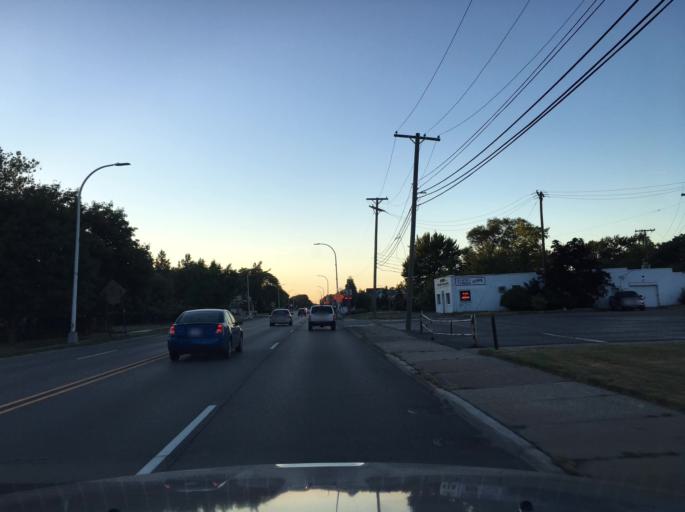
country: US
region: Michigan
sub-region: Macomb County
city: Fraser
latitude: 42.5347
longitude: -82.9504
